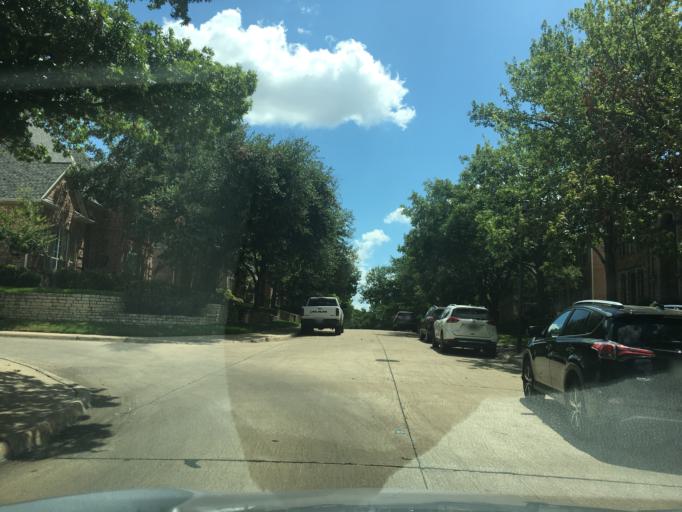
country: US
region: Texas
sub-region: Dallas County
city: Richardson
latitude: 32.8705
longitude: -96.7162
